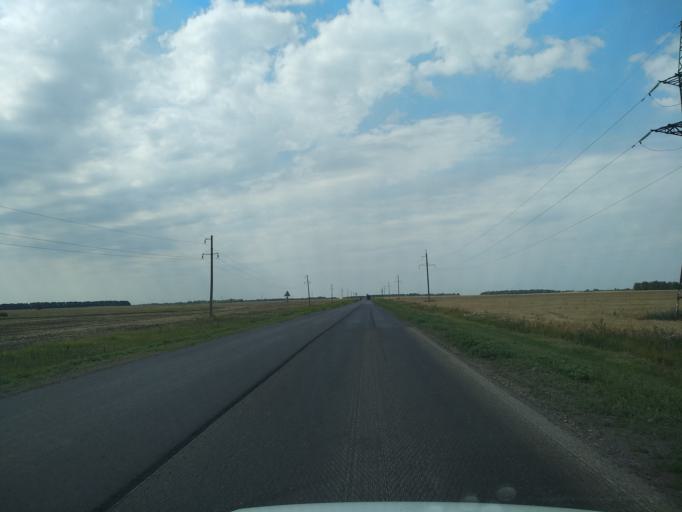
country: RU
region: Voronezj
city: Pereleshino
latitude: 51.7918
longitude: 40.1467
